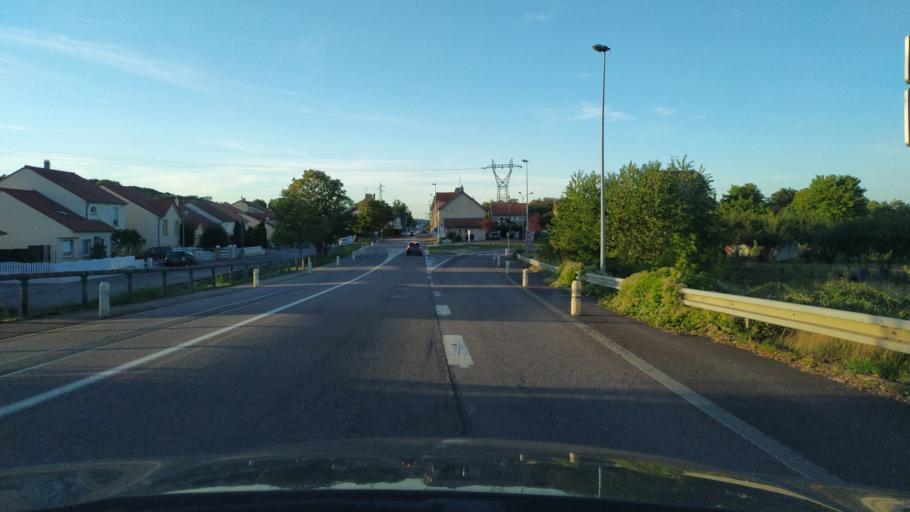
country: FR
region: Lorraine
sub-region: Departement de la Moselle
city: Maizieres-les-Metz
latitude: 49.2083
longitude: 6.1486
